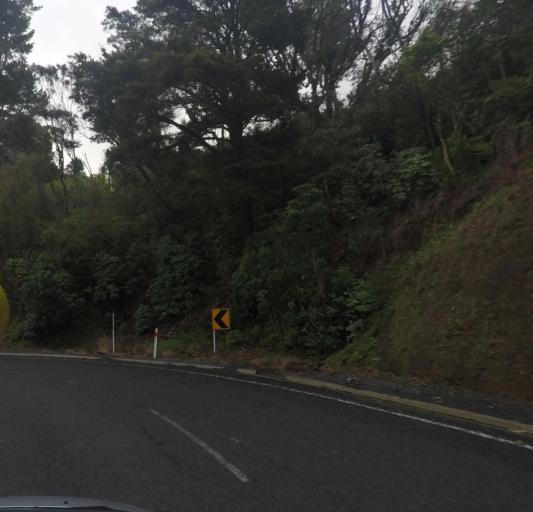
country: NZ
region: Auckland
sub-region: Auckland
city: Warkworth
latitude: -36.3748
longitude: 174.8080
